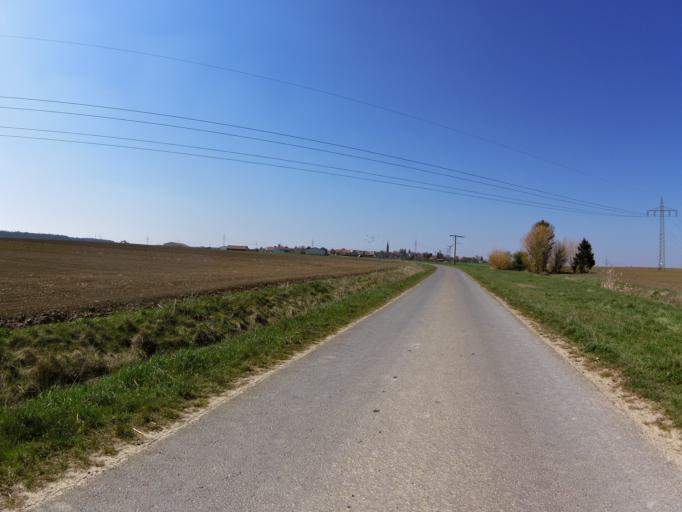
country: DE
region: Bavaria
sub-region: Regierungsbezirk Unterfranken
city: Biebelried
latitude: 49.7446
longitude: 10.0790
